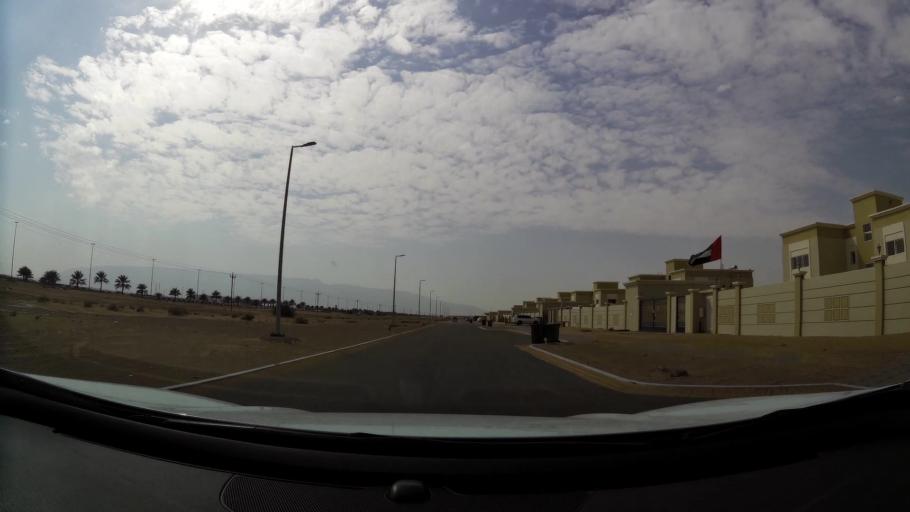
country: AE
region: Abu Dhabi
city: Al Ain
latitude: 24.0940
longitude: 55.8909
